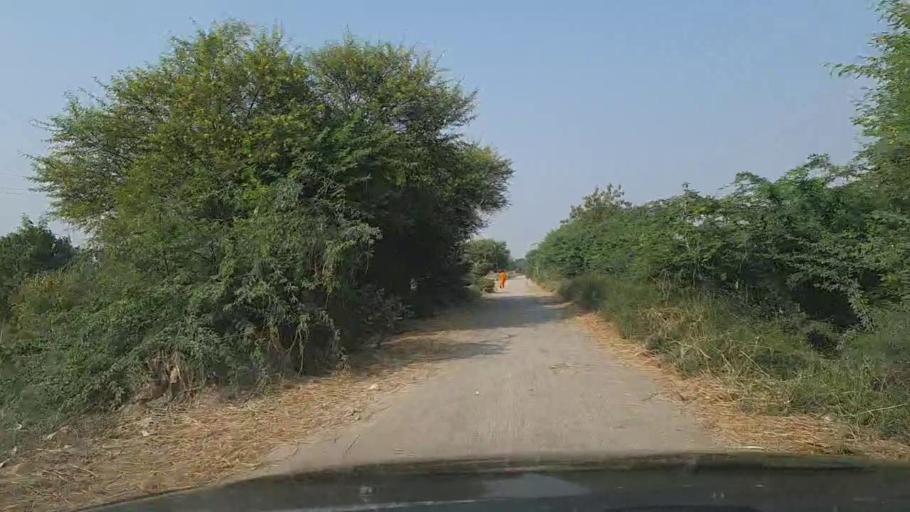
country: PK
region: Sindh
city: Mirpur Batoro
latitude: 24.7060
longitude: 68.2544
